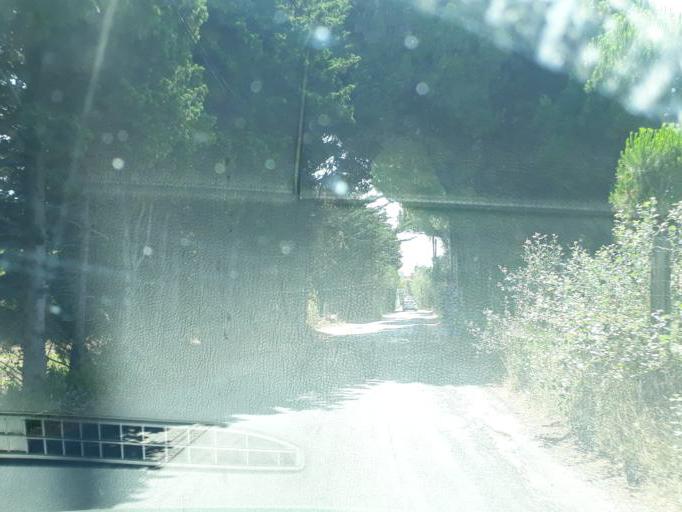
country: FR
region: Languedoc-Roussillon
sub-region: Departement de l'Herault
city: Le Cap d'Agde
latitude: 43.2821
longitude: 3.4906
